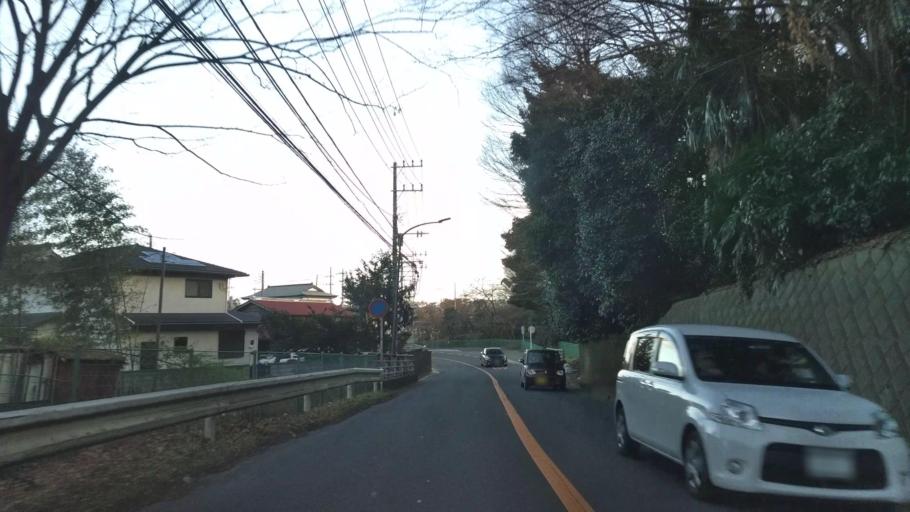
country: JP
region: Kanagawa
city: Oiso
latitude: 35.3443
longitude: 139.2888
